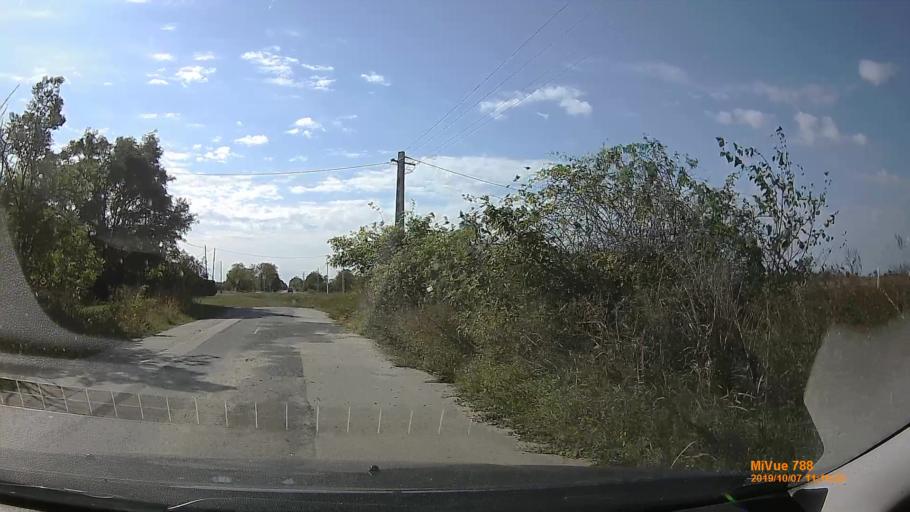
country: HU
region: Bekes
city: Kondoros
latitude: 46.7346
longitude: 20.7826
